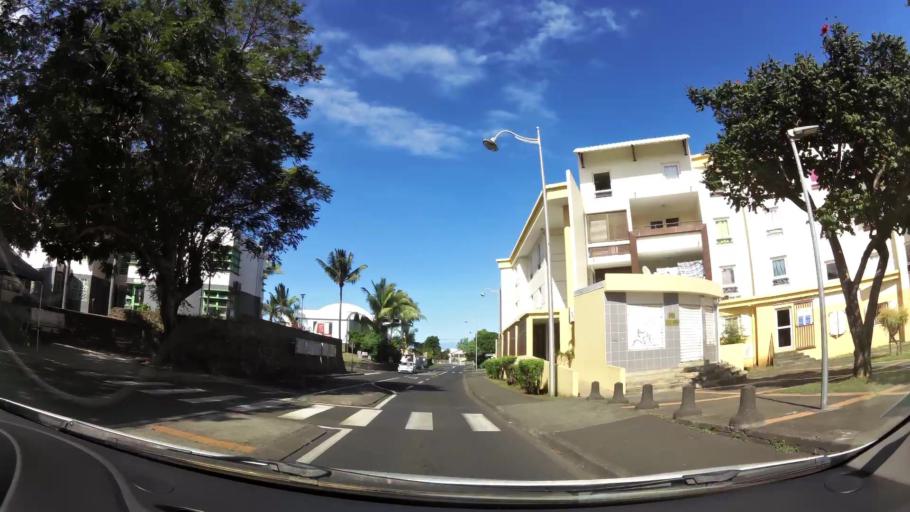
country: RE
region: Reunion
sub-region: Reunion
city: Saint-Pierre
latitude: -21.3291
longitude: 55.4787
